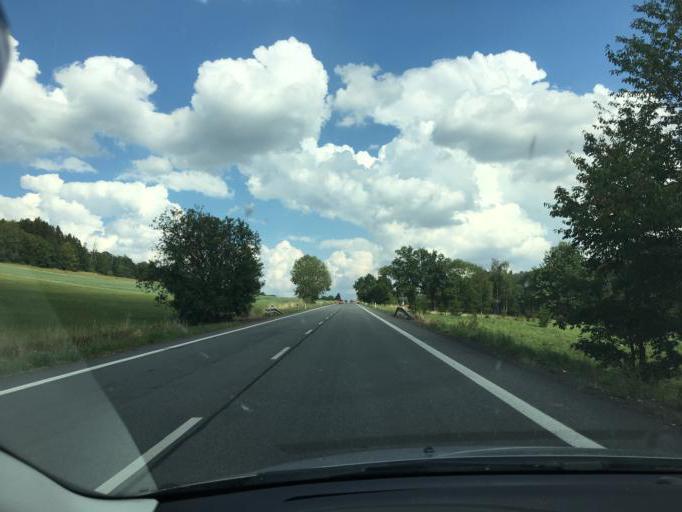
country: CZ
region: Liberecky
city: Jilemnice
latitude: 50.6229
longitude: 15.5370
